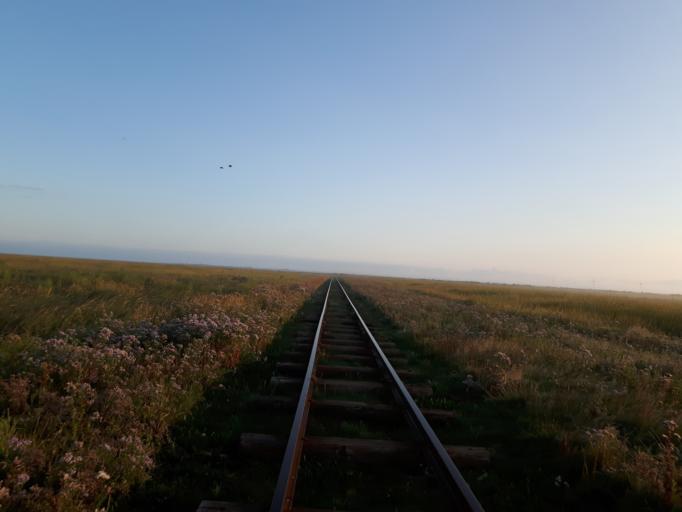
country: DE
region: Schleswig-Holstein
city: Dagebull
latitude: 54.6823
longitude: 8.7098
